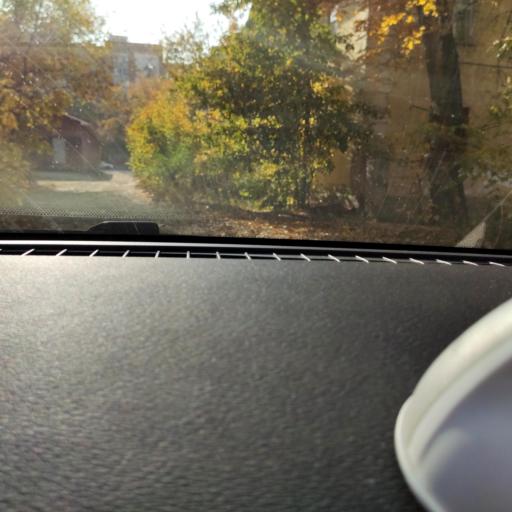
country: RU
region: Samara
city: Samara
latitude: 53.2013
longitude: 50.1532
